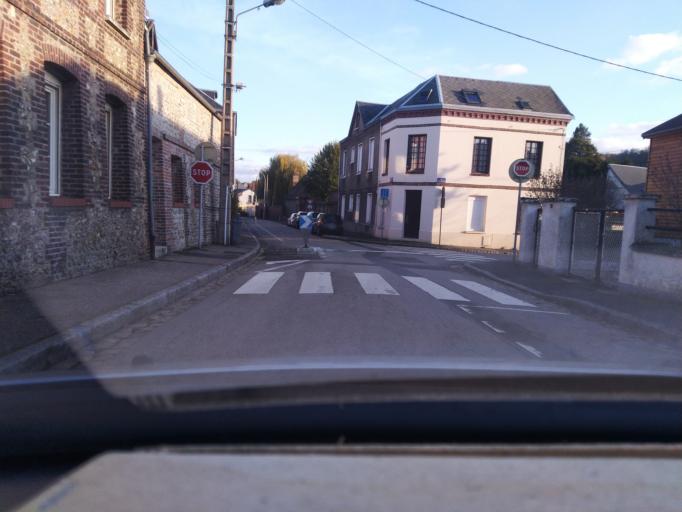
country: FR
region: Haute-Normandie
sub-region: Departement de la Seine-Maritime
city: Darnetal
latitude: 49.4379
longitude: 1.1397
